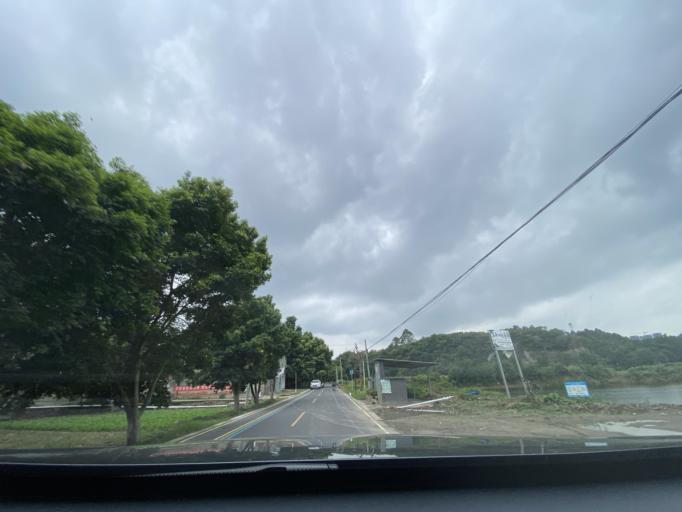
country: CN
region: Sichuan
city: Dongsheng
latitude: 30.4088
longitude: 103.9979
